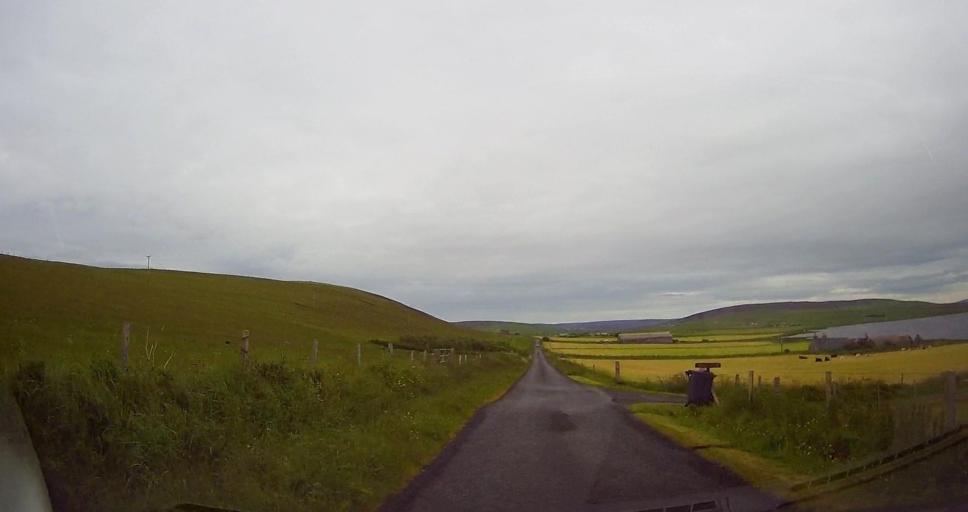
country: GB
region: Scotland
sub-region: Orkney Islands
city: Stromness
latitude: 59.1196
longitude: -3.2713
